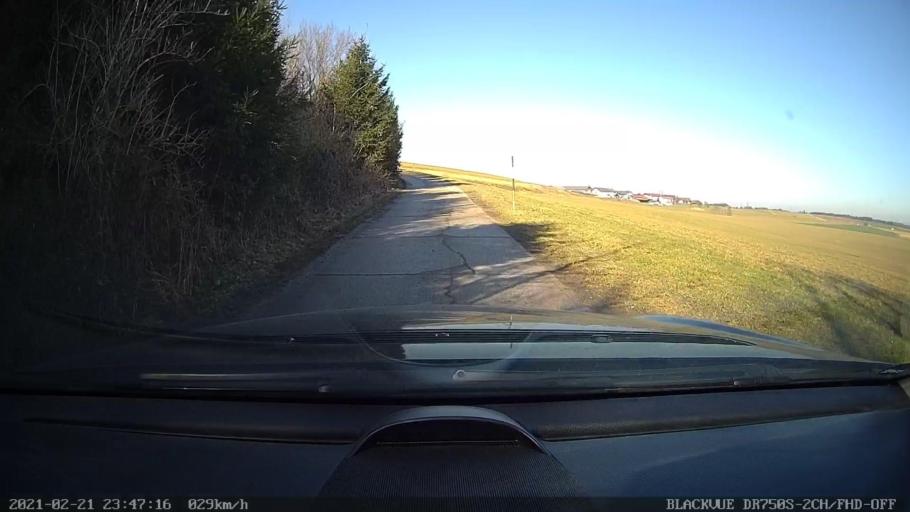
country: DE
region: Bavaria
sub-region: Upper Bavaria
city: Griesstatt
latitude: 47.9947
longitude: 12.2091
